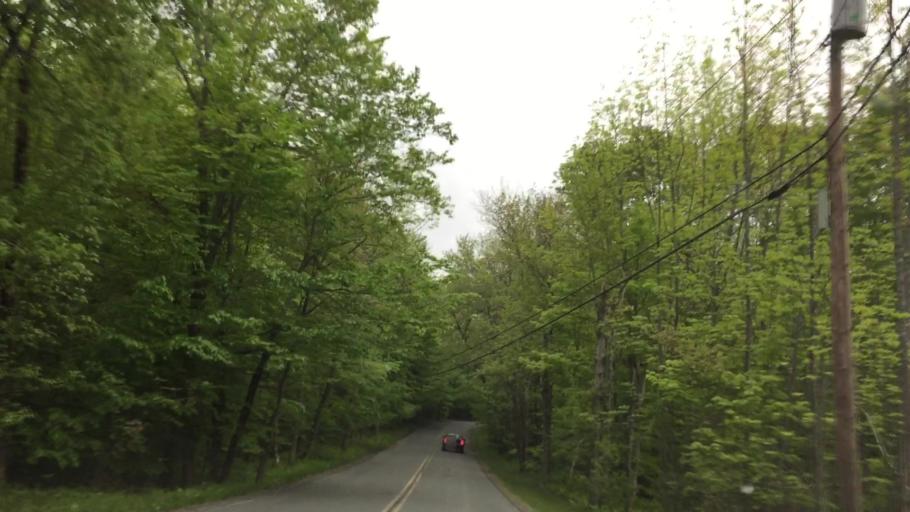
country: US
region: Massachusetts
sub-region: Berkshire County
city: Becket
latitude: 42.2813
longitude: -73.0474
